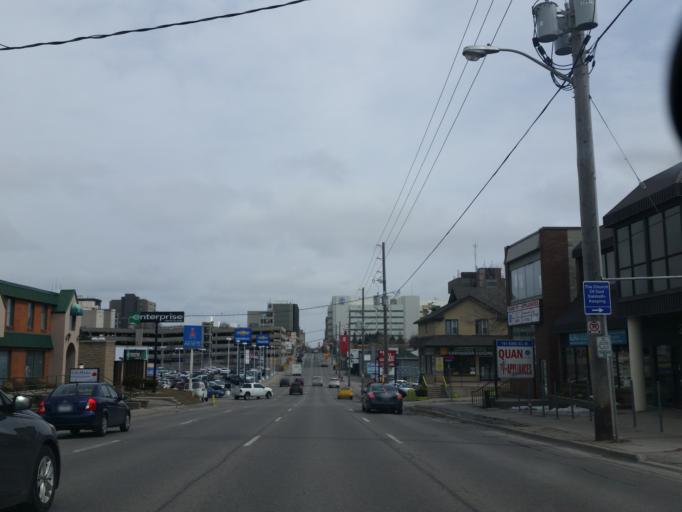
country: CA
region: Ontario
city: Oshawa
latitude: 43.8959
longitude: -78.8712
